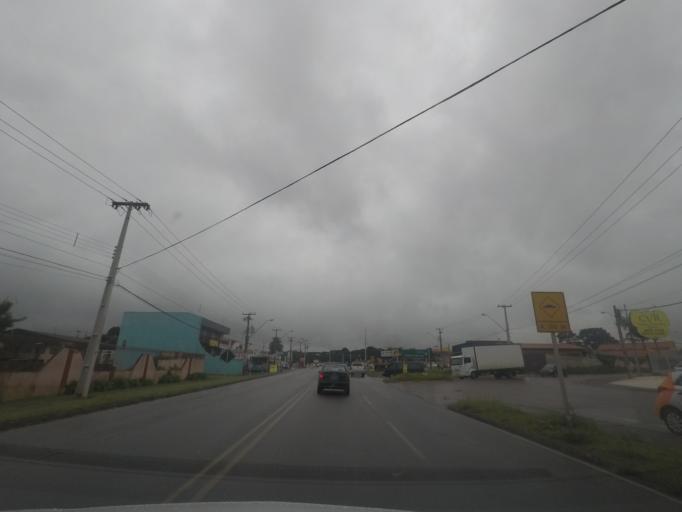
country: BR
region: Parana
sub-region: Colombo
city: Colombo
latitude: -25.3495
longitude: -49.1645
